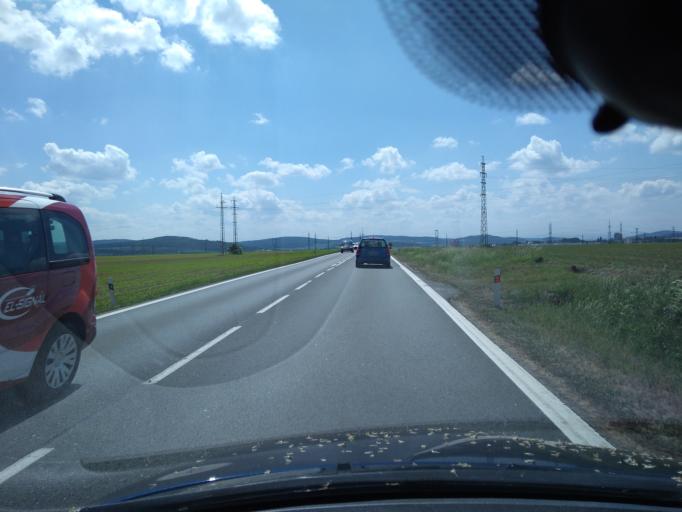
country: CZ
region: Plzensky
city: Prestice
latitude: 49.5961
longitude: 13.3267
